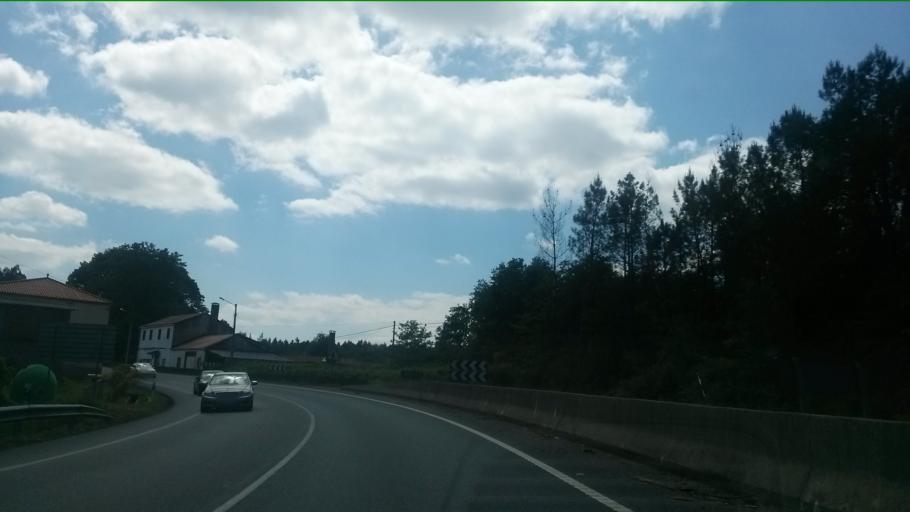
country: ES
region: Galicia
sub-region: Provincia da Coruna
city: Touro
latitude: 42.9489
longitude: -8.3354
